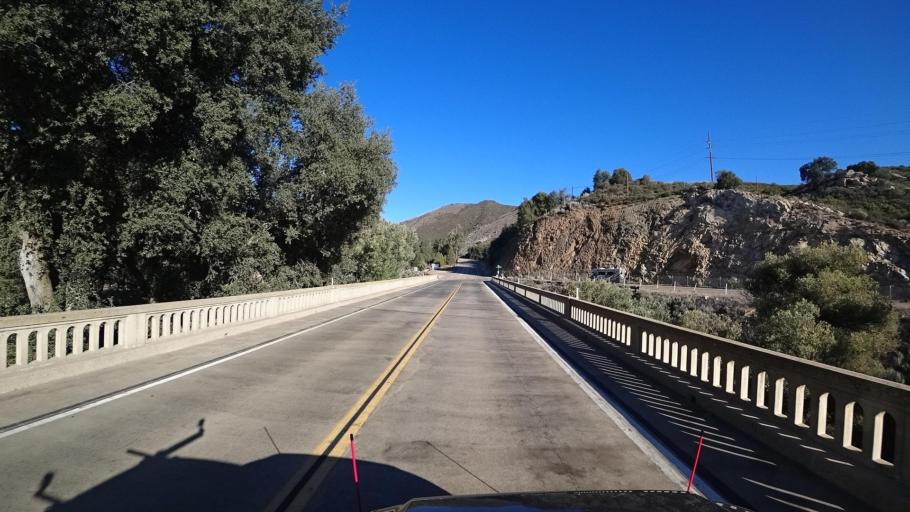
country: US
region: California
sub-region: San Diego County
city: Pine Valley
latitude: 32.8376
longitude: -116.5373
